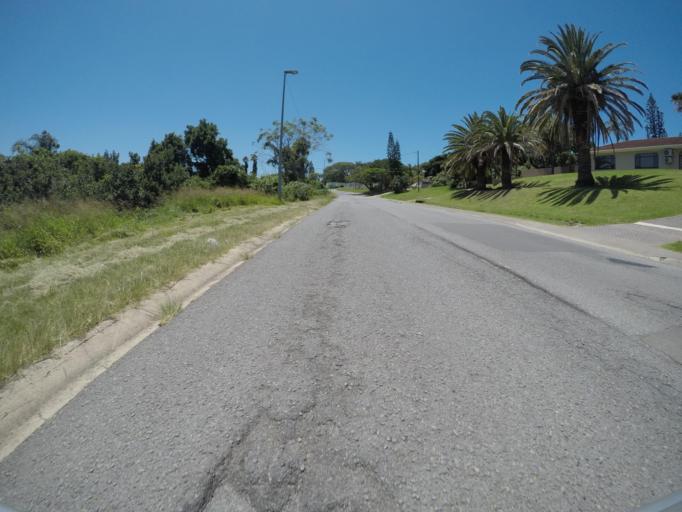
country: ZA
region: Eastern Cape
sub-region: Buffalo City Metropolitan Municipality
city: East London
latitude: -32.9789
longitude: 27.9397
